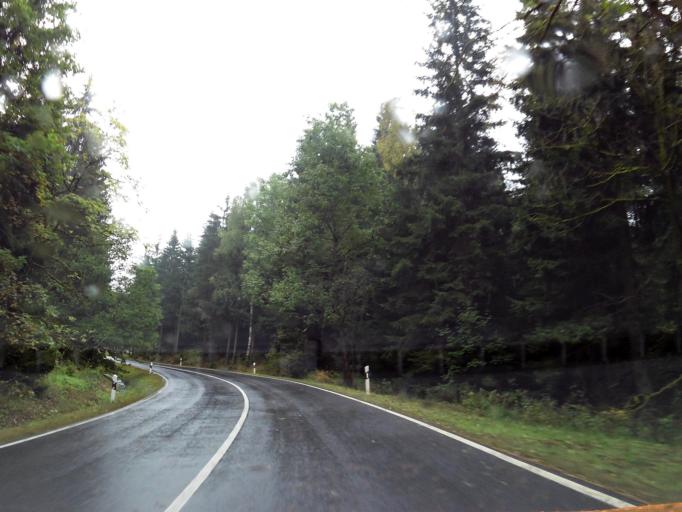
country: DE
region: Saxony-Anhalt
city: Harzgerode
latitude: 51.6458
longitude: 11.1196
